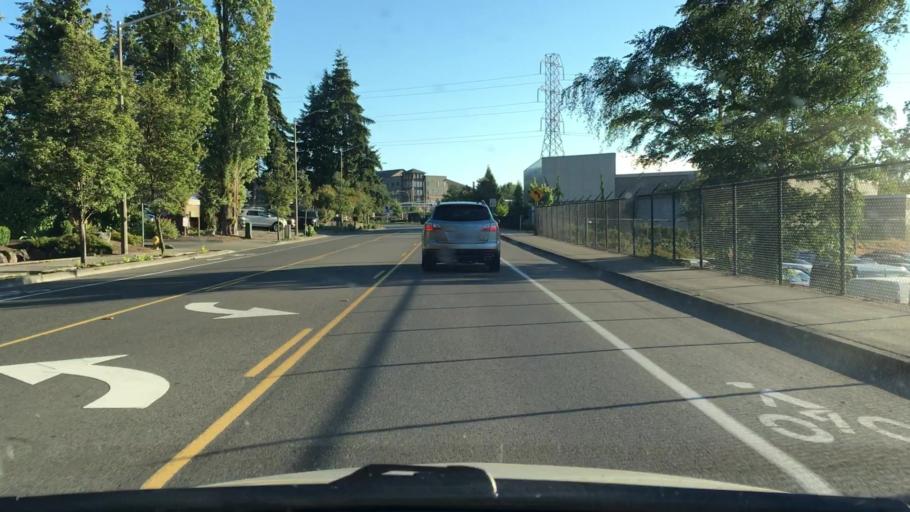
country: US
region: Washington
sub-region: King County
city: Kingsgate
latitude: 47.7061
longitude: -122.1733
